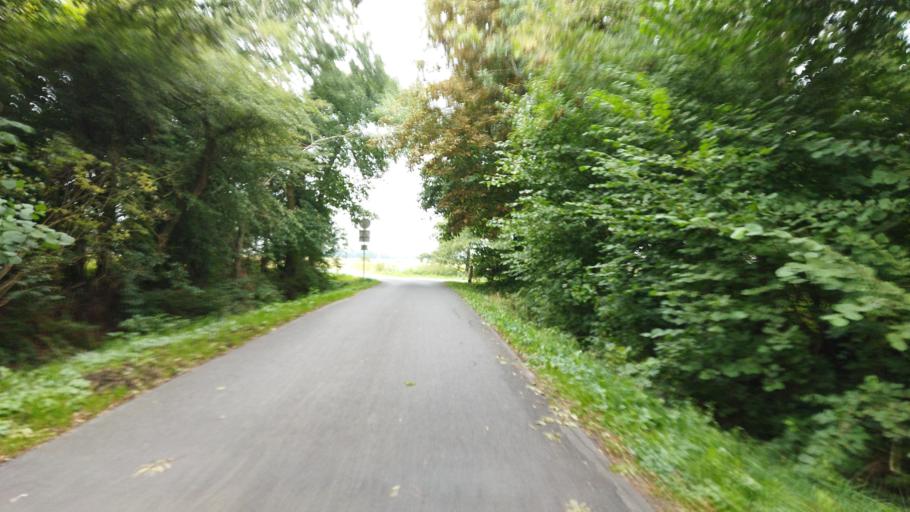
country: DE
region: Lower Saxony
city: Leer
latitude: 53.2427
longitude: 7.4417
